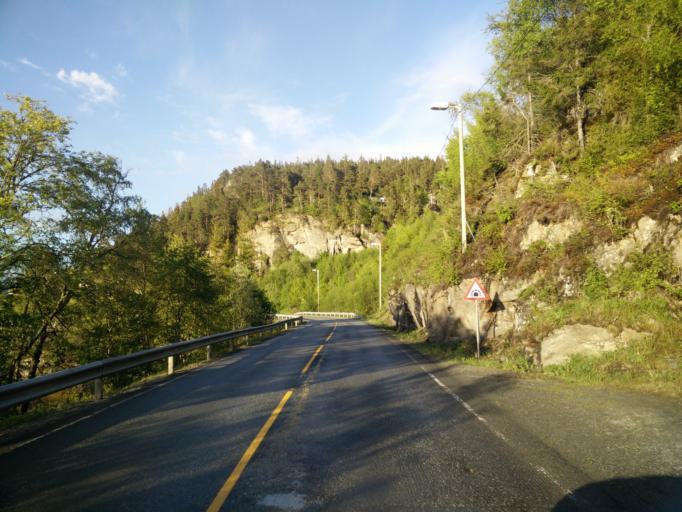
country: NO
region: Sor-Trondelag
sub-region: Skaun
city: Borsa
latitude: 63.3260
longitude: 10.0922
